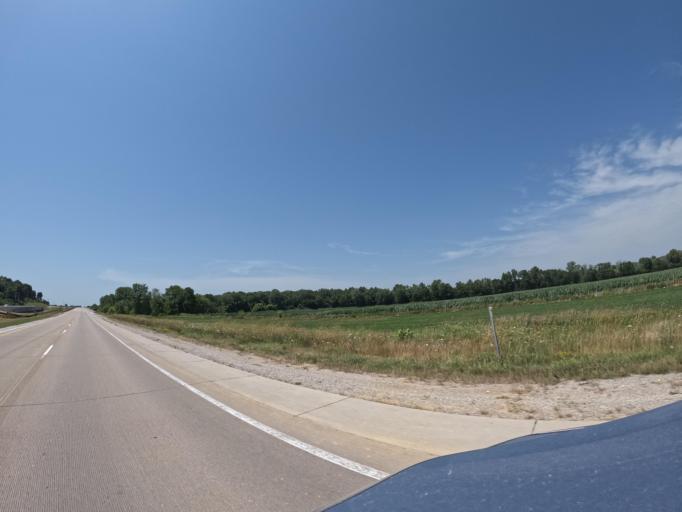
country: US
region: Iowa
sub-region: Henry County
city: Mount Pleasant
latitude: 40.9756
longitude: -91.6755
